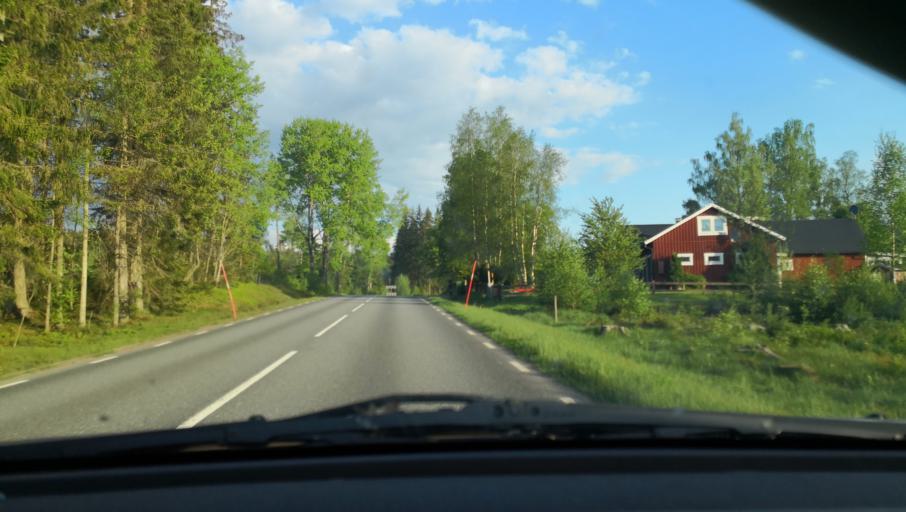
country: SE
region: Joenkoeping
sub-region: Vetlanda Kommun
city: Landsbro
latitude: 57.3896
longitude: 14.8297
